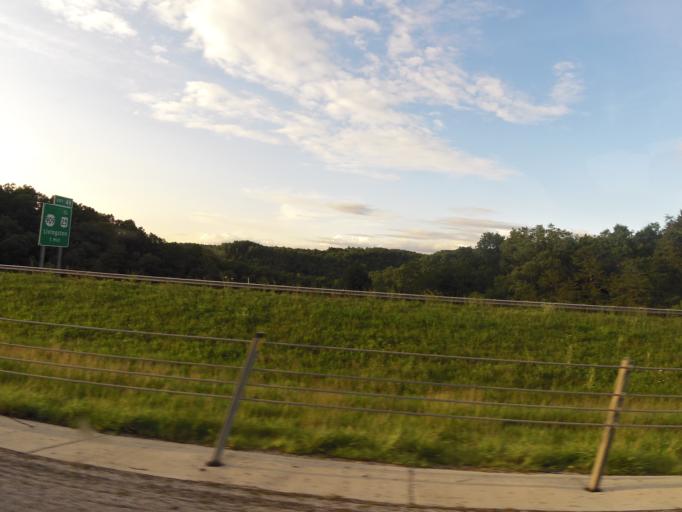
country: US
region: Kentucky
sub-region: Laurel County
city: London
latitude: 37.2144
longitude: -84.1983
